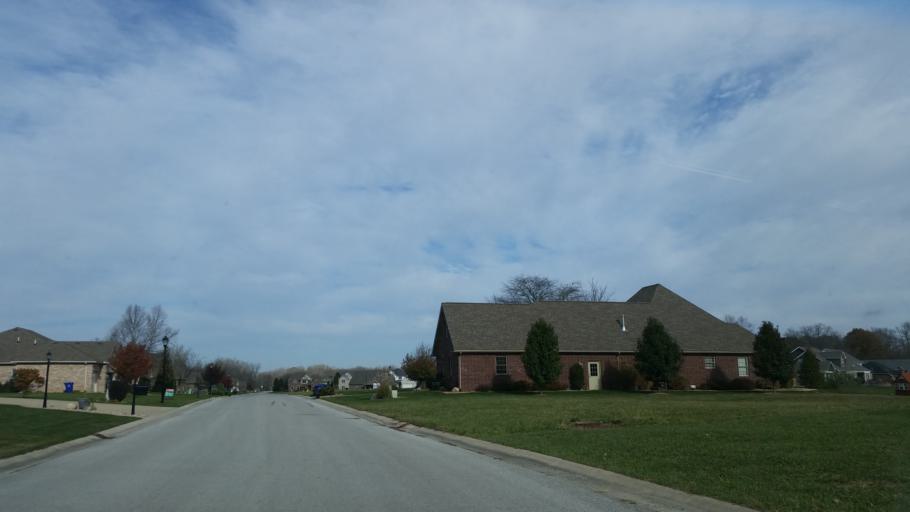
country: US
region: Indiana
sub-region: Howard County
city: Indian Heights
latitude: 40.4269
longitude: -86.1559
